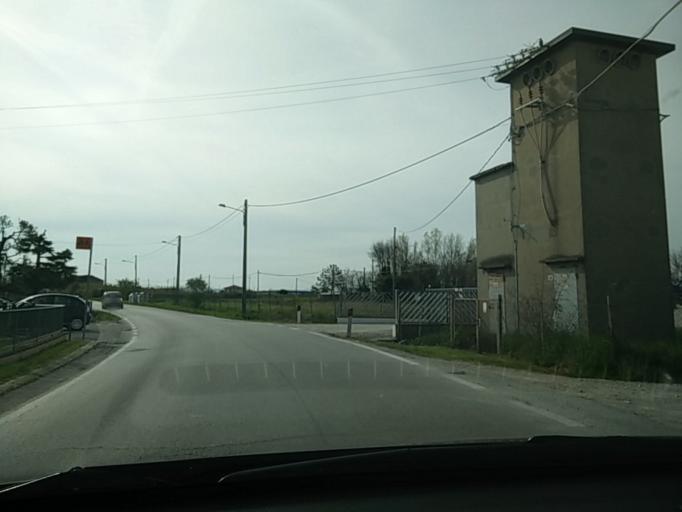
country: IT
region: Emilia-Romagna
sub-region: Provincia di Rimini
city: Santa Giustina
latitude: 44.0867
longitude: 12.4775
